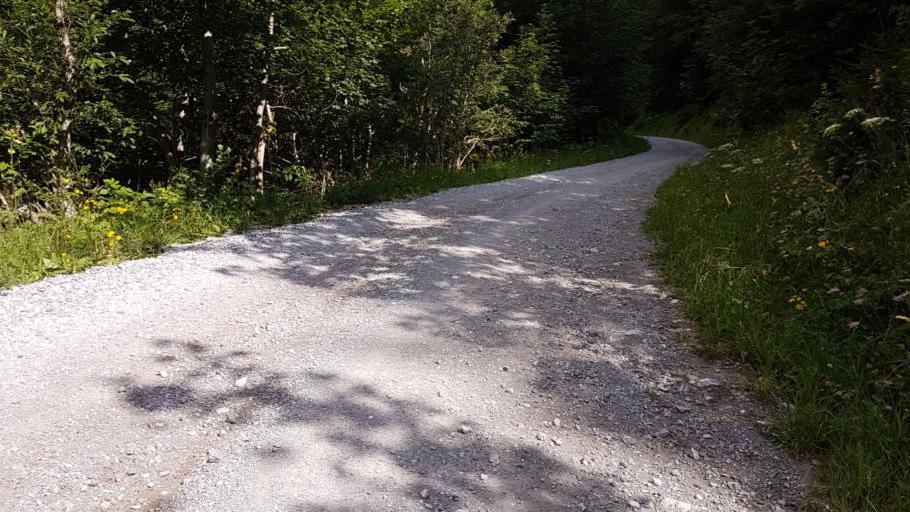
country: CH
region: Bern
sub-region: Obersimmental-Saanen District
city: Boltigen
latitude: 46.6849
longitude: 7.4482
